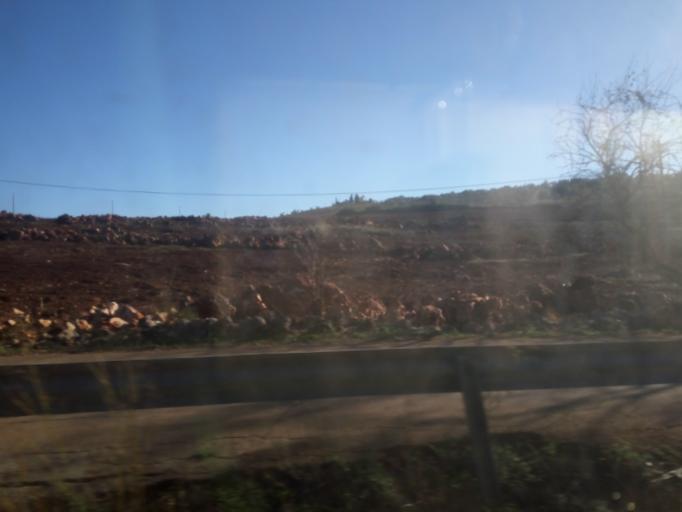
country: PT
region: Faro
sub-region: Silves
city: Sao Bartolomeu de Messines
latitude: 37.2473
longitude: -8.2914
